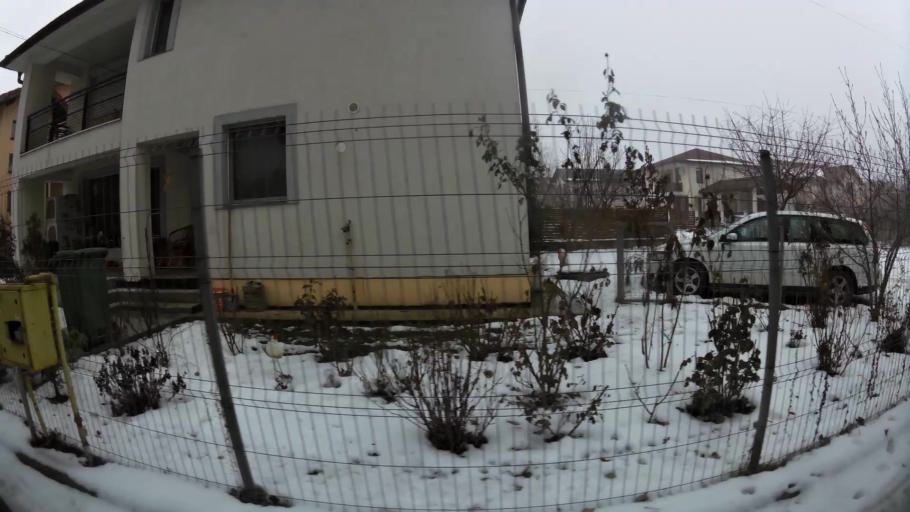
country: RO
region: Ilfov
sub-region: Comuna Chiajna
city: Rosu
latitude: 44.4443
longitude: 25.9995
